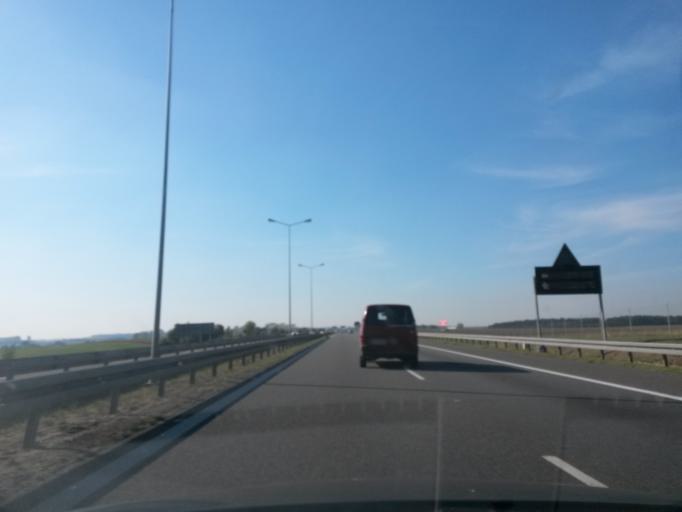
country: PL
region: Opole Voivodeship
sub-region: Powiat strzelecki
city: Ujazd
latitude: 50.4472
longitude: 18.3405
